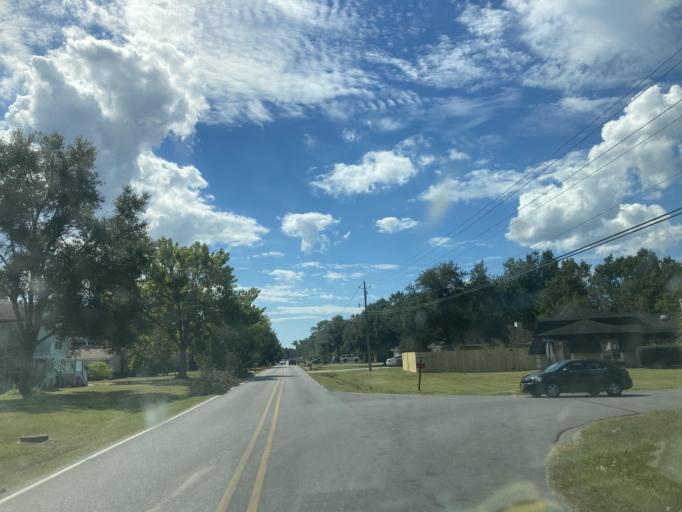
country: US
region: Mississippi
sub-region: Jackson County
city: Saint Martin
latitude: 30.4390
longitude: -88.8539
